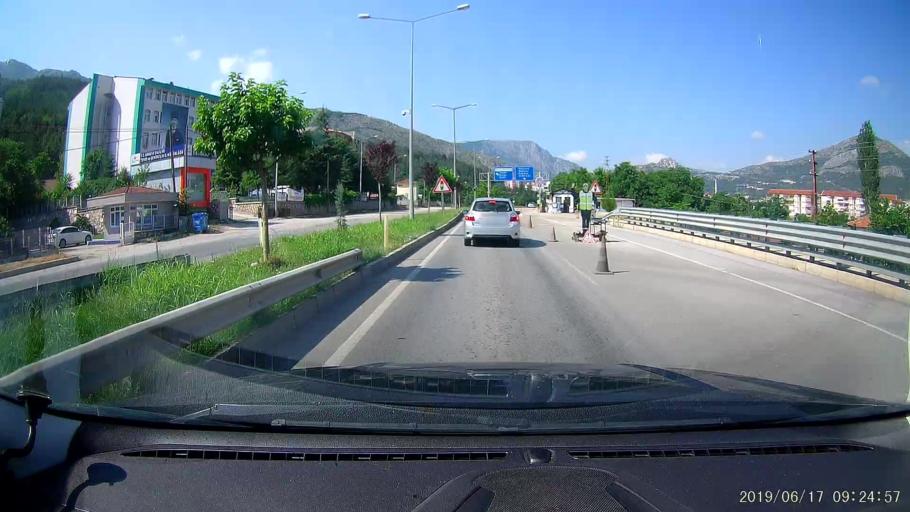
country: TR
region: Amasya
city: Amasya
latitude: 40.6691
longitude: 35.8526
